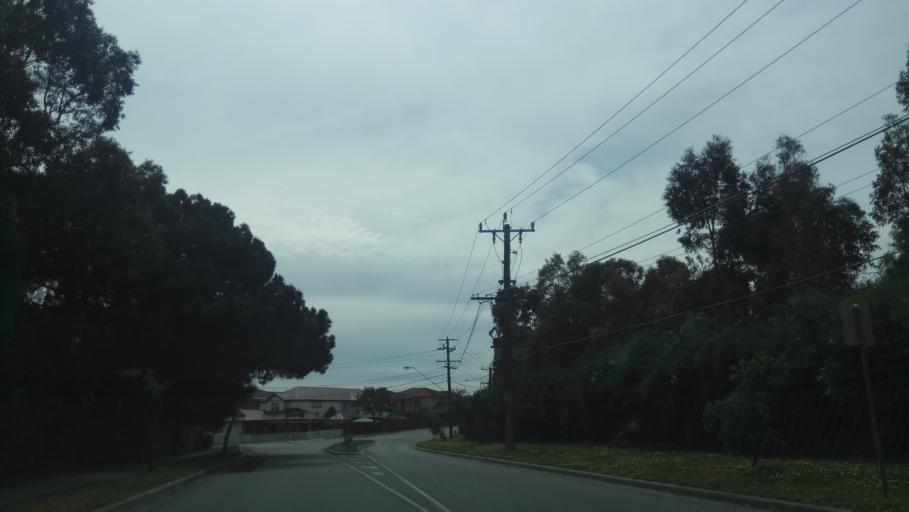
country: AU
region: Victoria
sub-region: Kingston
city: Dingley Village
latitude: -37.9727
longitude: 145.1331
